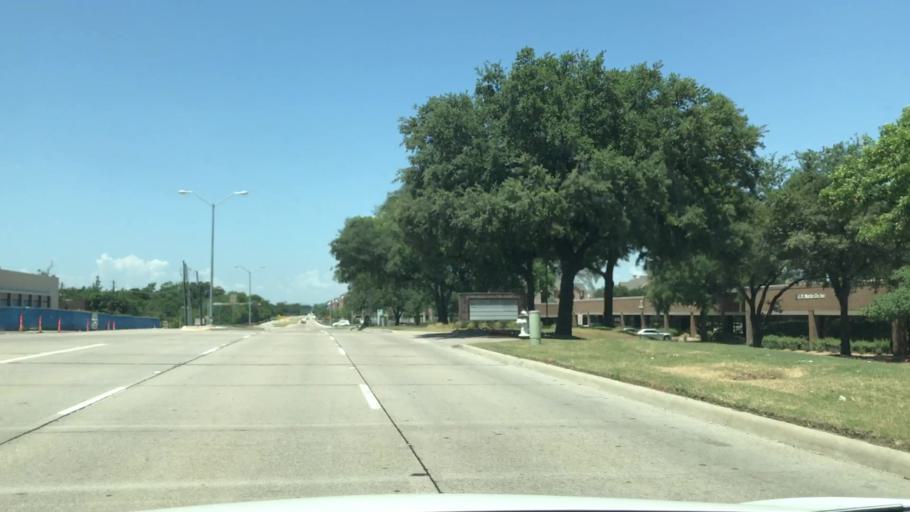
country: US
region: Texas
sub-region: Dallas County
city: Farmers Branch
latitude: 32.8956
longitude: -96.9162
